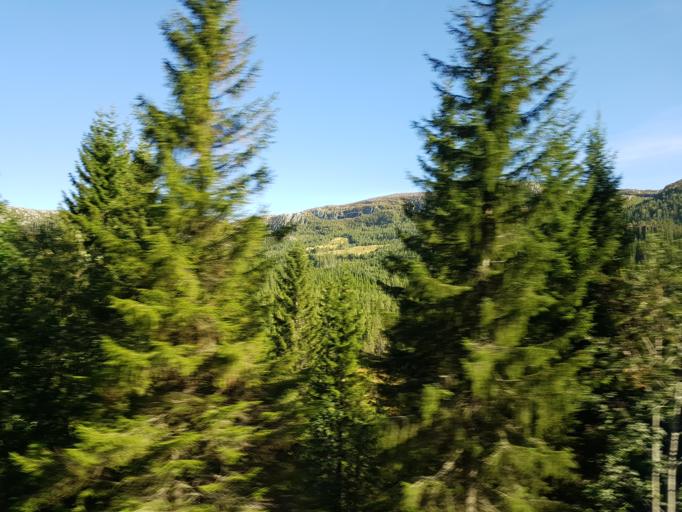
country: NO
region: Sor-Trondelag
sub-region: Afjord
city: A i Afjord
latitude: 63.7262
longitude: 10.2348
